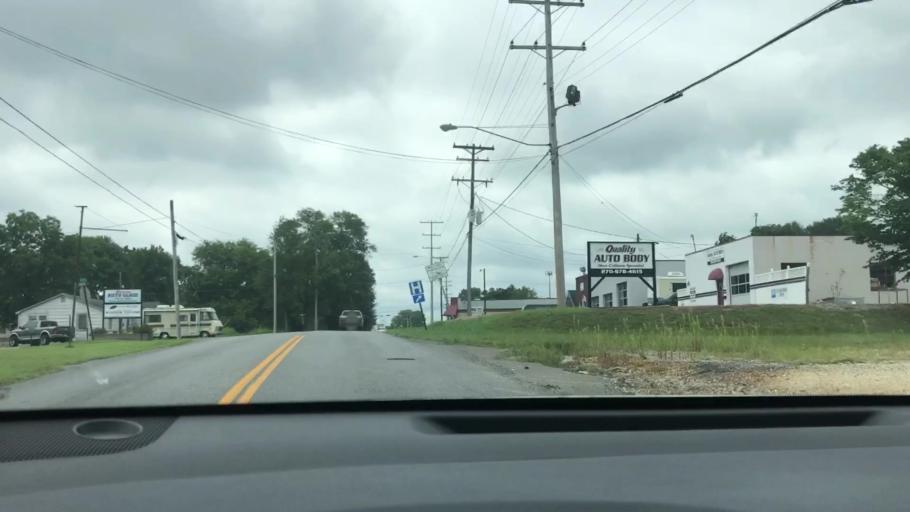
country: US
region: Kentucky
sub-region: Calloway County
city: Murray
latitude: 36.6048
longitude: -88.3023
